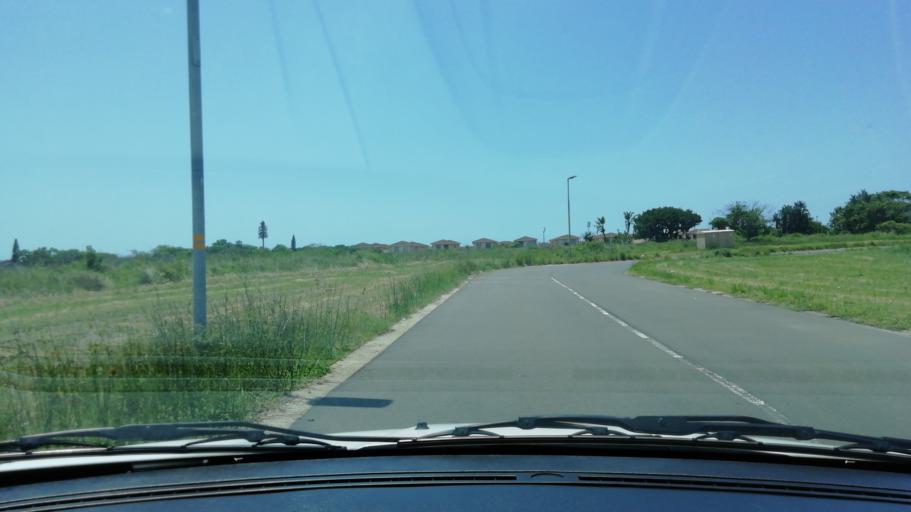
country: ZA
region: KwaZulu-Natal
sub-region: uThungulu District Municipality
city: Richards Bay
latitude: -28.7390
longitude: 32.0478
